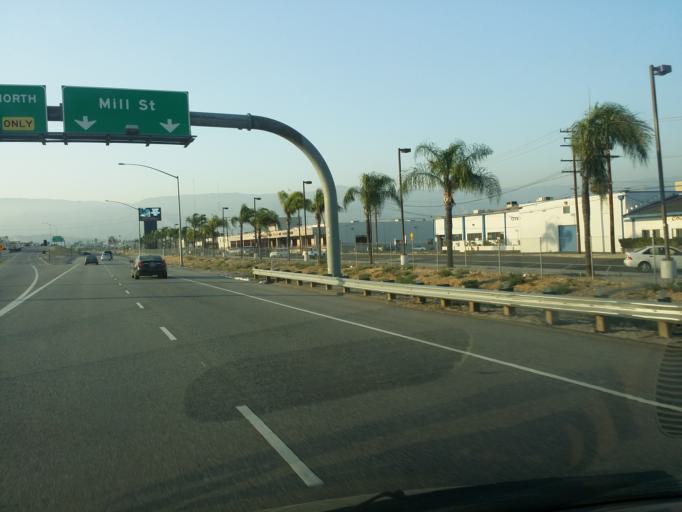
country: US
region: California
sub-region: San Bernardino County
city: Colton
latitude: 34.0879
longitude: -117.3014
